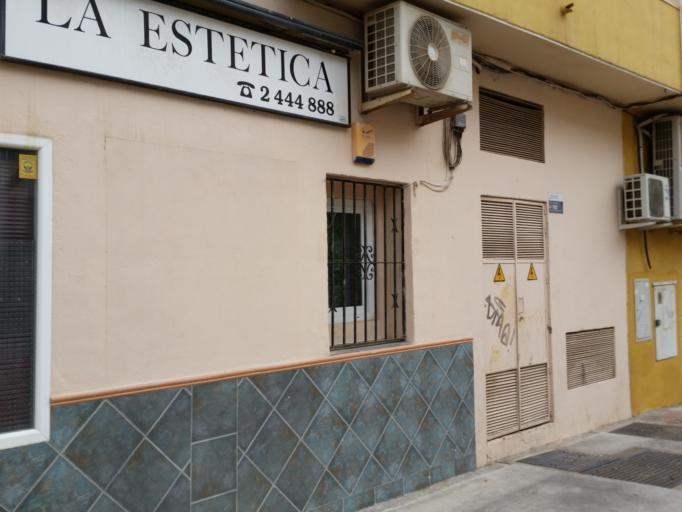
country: ES
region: Andalusia
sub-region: Provincia de Malaga
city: Benalmadena
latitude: 36.5985
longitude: -4.5355
